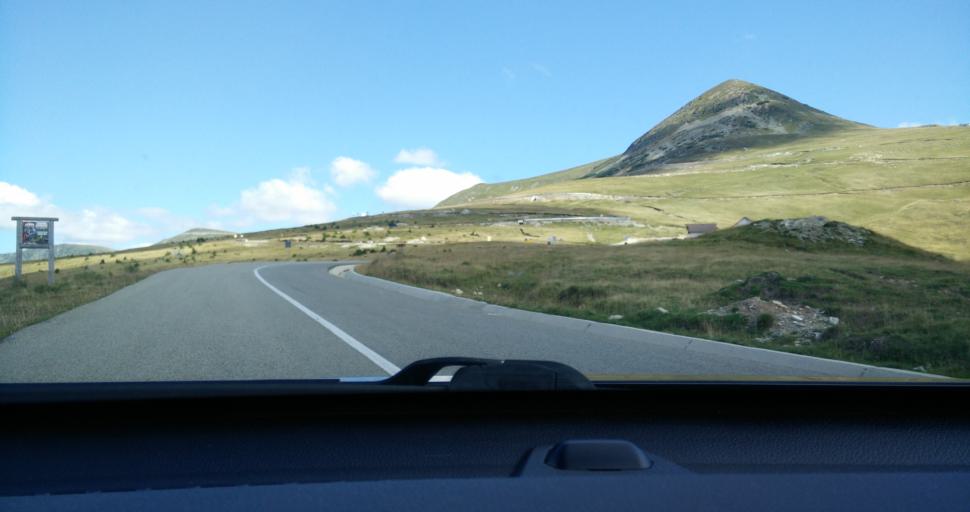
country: RO
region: Gorj
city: Novaci-Straini
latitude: 45.3119
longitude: 23.6828
